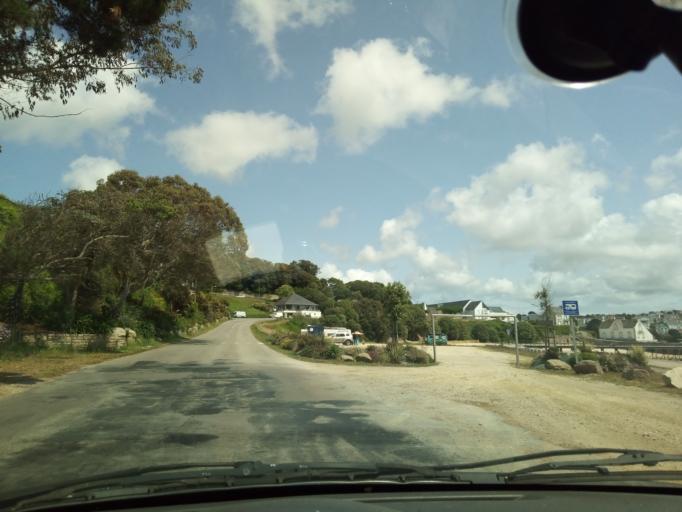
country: FR
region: Brittany
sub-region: Departement du Finistere
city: Audierne
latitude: 48.0160
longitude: -4.5384
